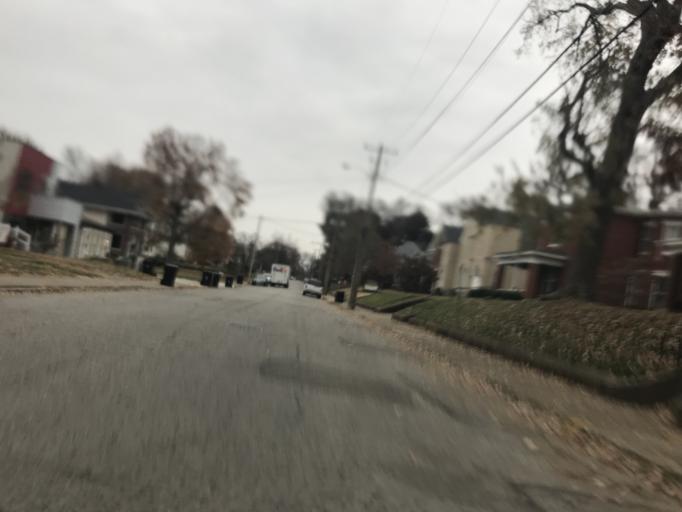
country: US
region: Indiana
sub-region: Clark County
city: Jeffersonville
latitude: 38.2548
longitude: -85.7082
